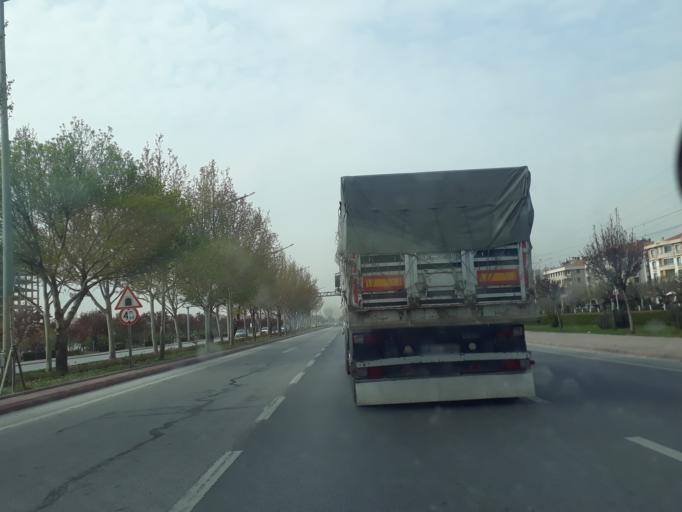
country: TR
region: Konya
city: Selcuklu
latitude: 37.9641
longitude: 32.5147
